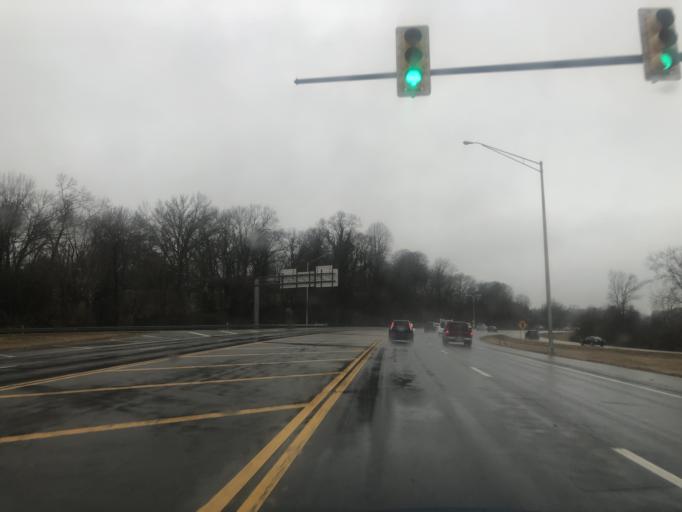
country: US
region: Tennessee
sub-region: Davidson County
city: Oak Hill
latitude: 36.1093
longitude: -86.7232
